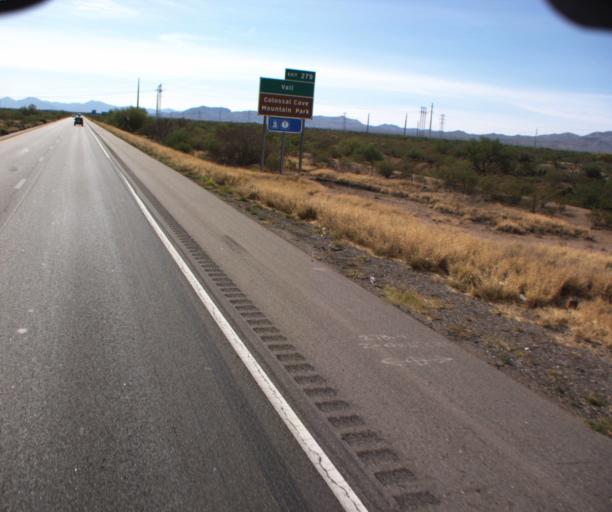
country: US
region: Arizona
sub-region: Pima County
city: Vail
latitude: 32.0360
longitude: -110.7342
